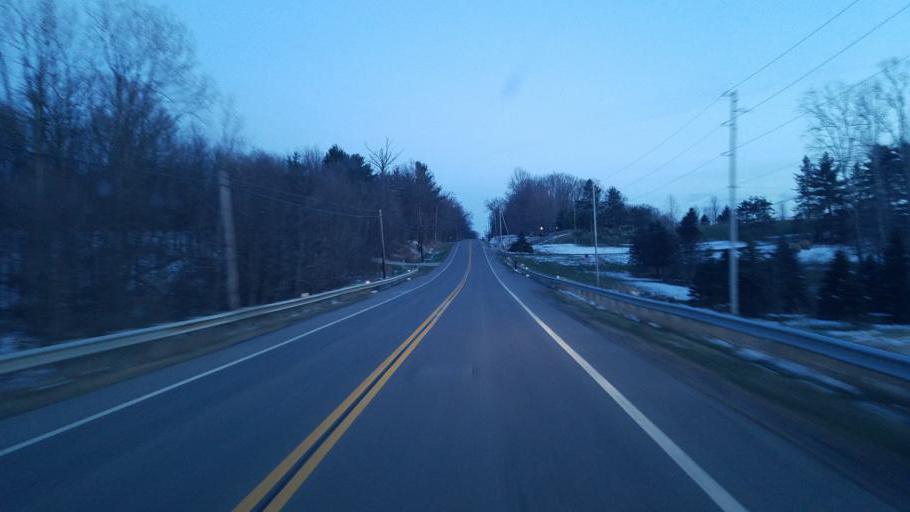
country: US
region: Ohio
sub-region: Ashland County
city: Ashland
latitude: 40.8187
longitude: -82.2791
